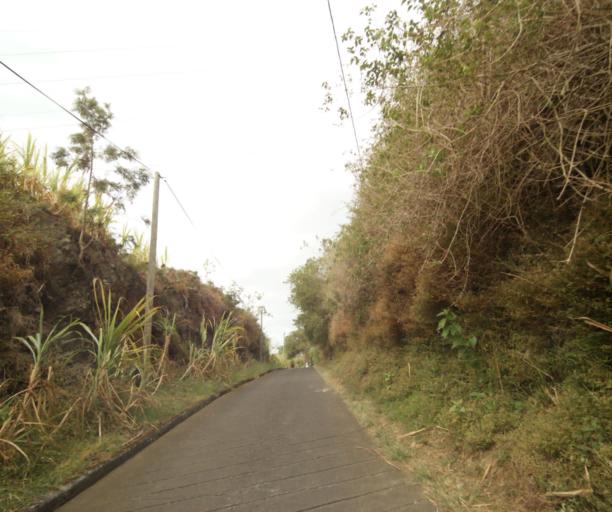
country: RE
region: Reunion
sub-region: Reunion
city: Saint-Paul
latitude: -21.0300
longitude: 55.3161
